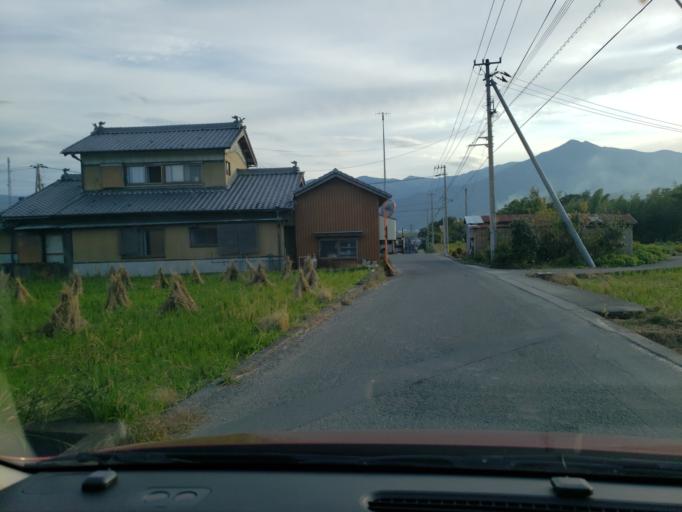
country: JP
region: Tokushima
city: Wakimachi
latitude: 34.0790
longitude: 134.2283
